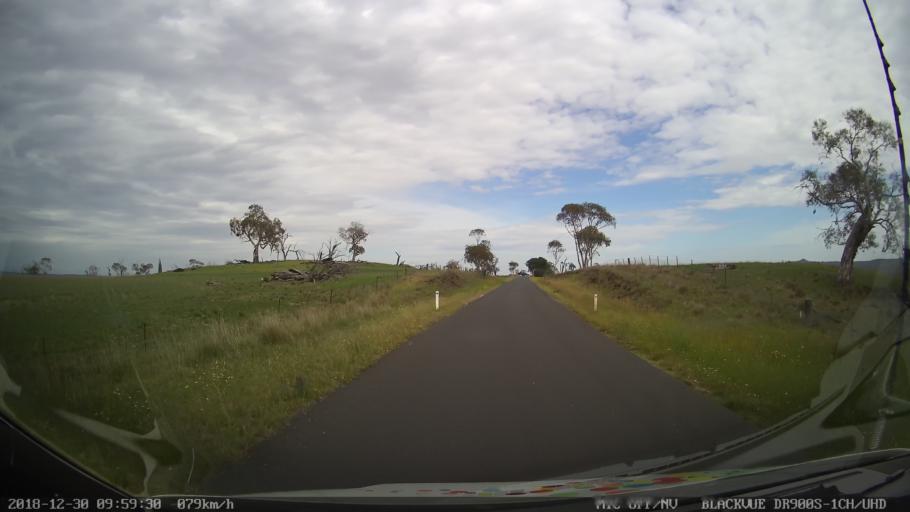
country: AU
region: New South Wales
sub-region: Cooma-Monaro
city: Cooma
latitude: -36.5231
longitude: 149.2094
